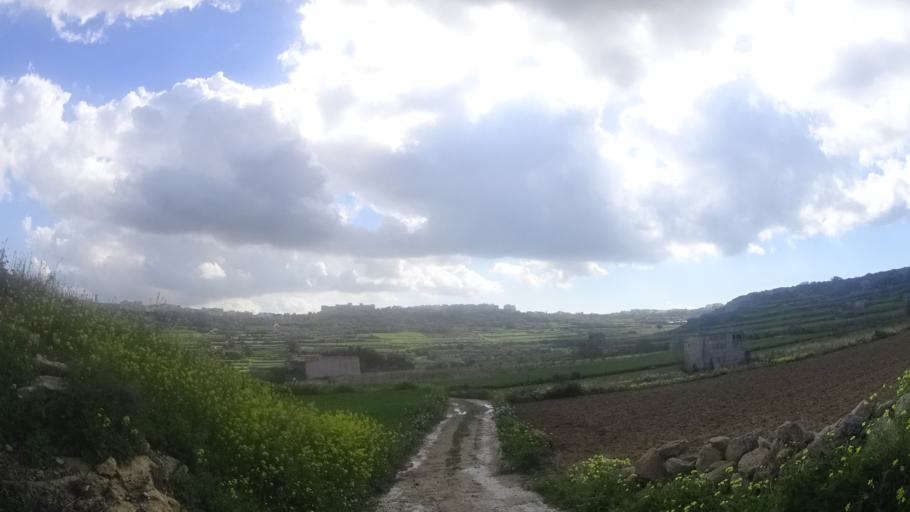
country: MT
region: L-Imtarfa
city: Imtarfa
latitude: 35.8979
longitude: 14.3886
